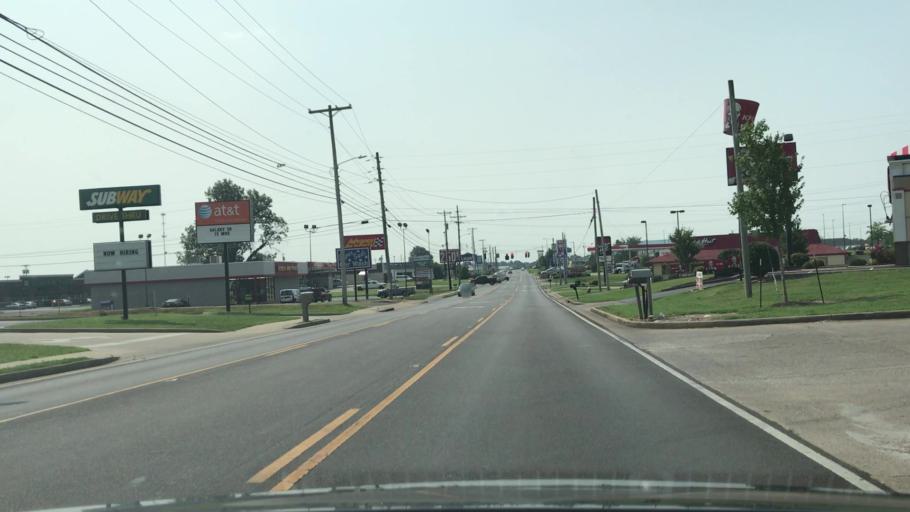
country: US
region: Kentucky
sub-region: Graves County
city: Mayfield
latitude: 36.7240
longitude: -88.6281
